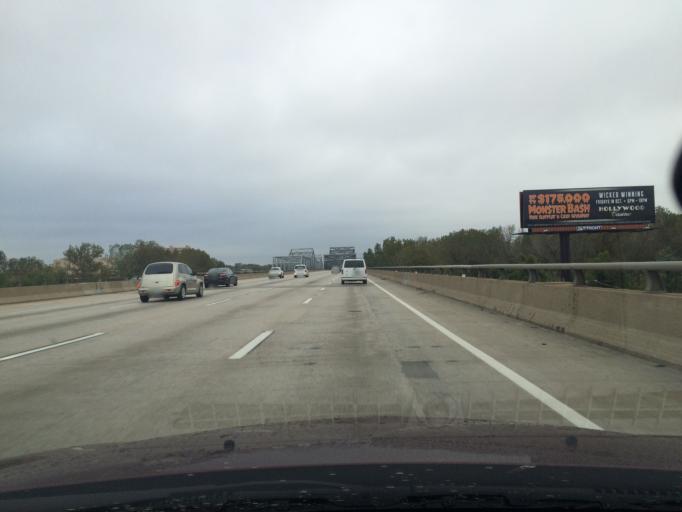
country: US
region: Missouri
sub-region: Saint Charles County
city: Saint Charles
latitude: 38.7665
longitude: -90.4893
